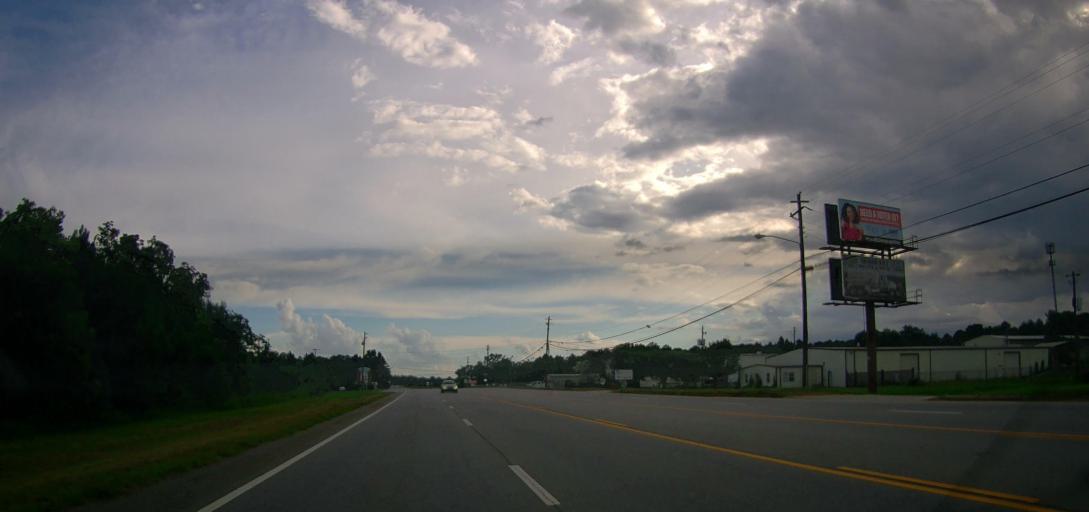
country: US
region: Georgia
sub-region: Peach County
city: Byron
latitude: 32.6466
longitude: -83.7614
